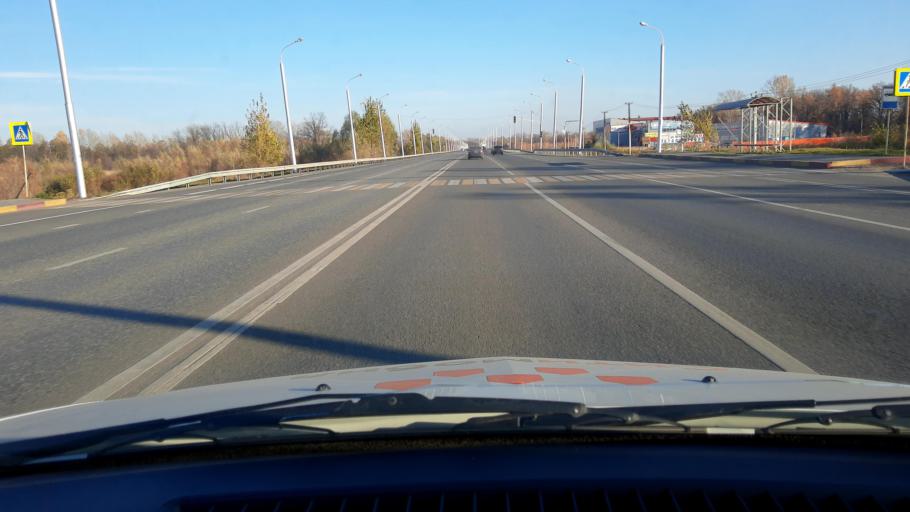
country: RU
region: Bashkortostan
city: Ufa
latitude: 54.8055
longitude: 56.1805
